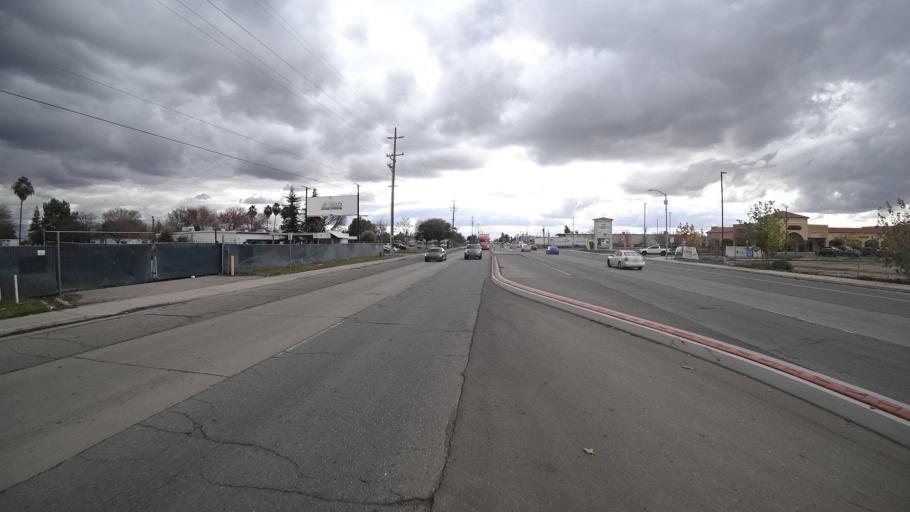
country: US
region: California
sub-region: Kern County
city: Bakersfield
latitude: 35.3223
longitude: -119.0030
